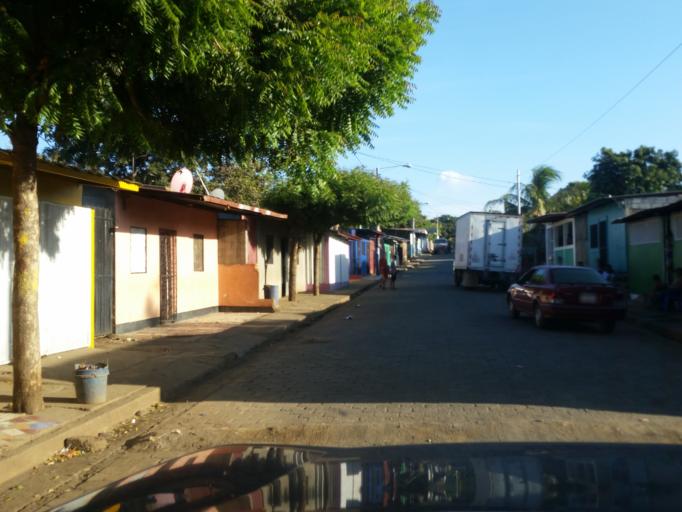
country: NI
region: Managua
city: Managua
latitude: 12.1082
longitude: -86.2404
